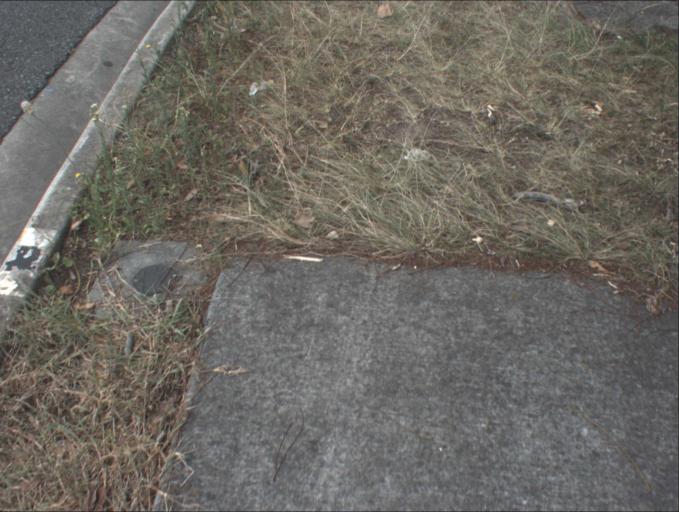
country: AU
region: Queensland
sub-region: Logan
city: Beenleigh
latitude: -27.7148
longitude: 153.1876
